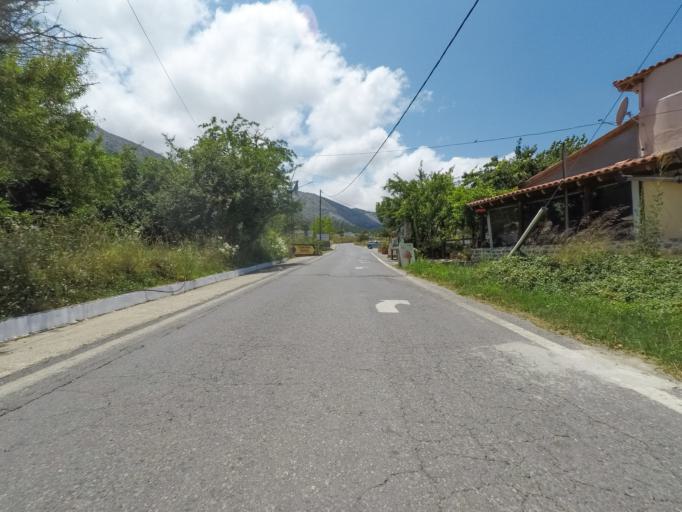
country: GR
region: Crete
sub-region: Nomos Irakleiou
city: Mokhos
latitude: 35.1702
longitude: 25.4433
